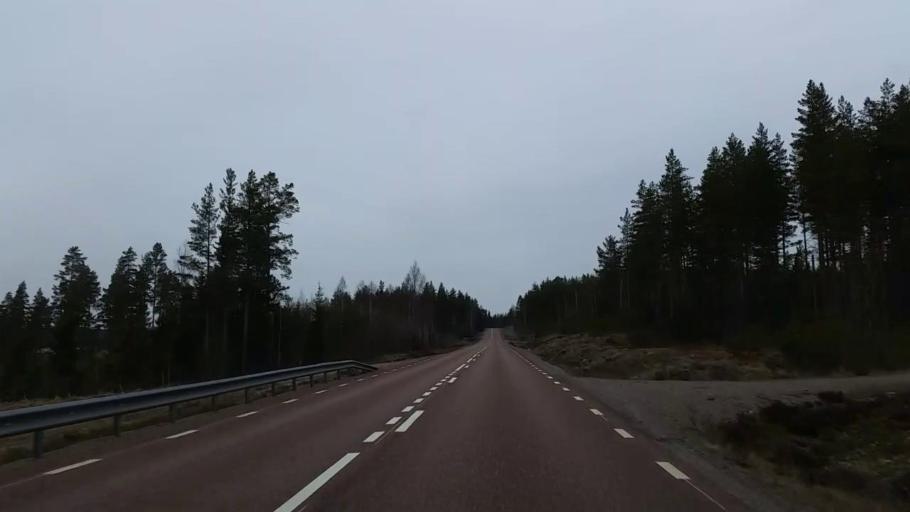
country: SE
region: Gaevleborg
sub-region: Ovanakers Kommun
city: Edsbyn
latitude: 61.2197
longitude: 15.8771
